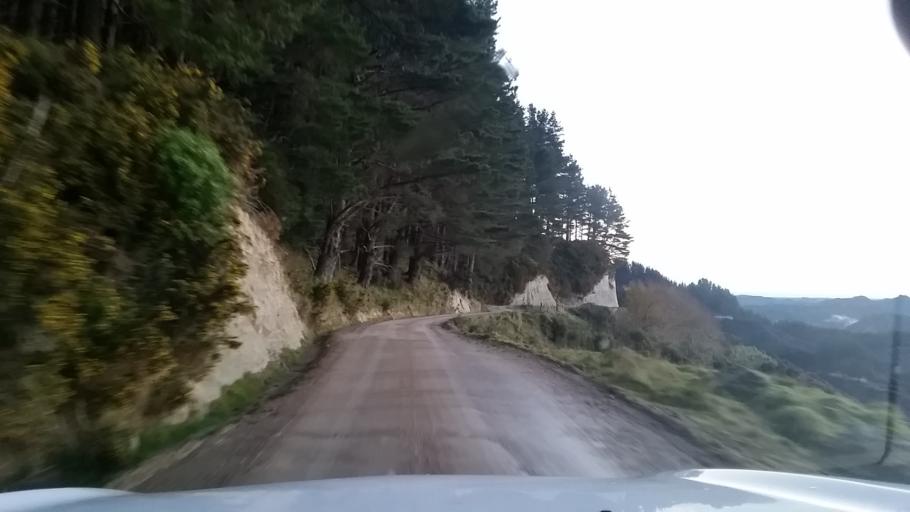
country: NZ
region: Manawatu-Wanganui
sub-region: Wanganui District
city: Wanganui
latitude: -39.7621
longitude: 174.8792
